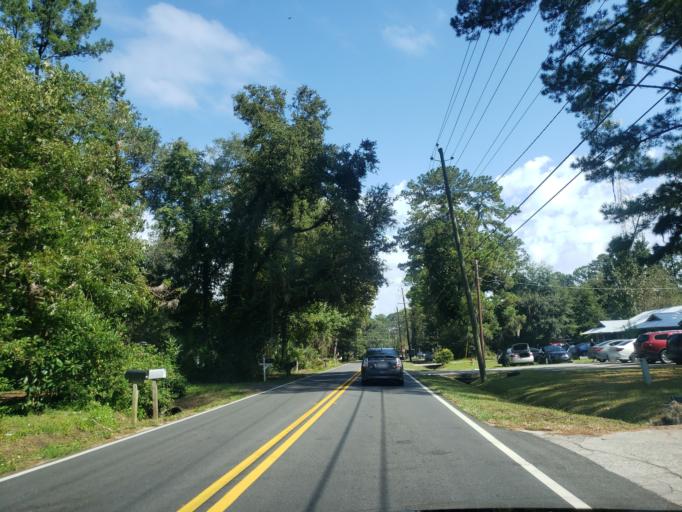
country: US
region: Georgia
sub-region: Chatham County
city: Montgomery
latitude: 31.9543
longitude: -81.1026
